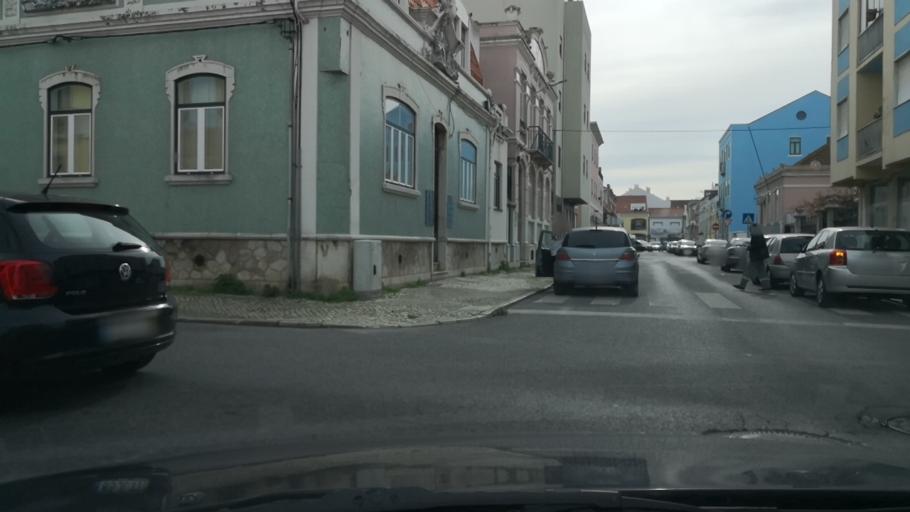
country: PT
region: Setubal
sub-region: Setubal
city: Setubal
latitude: 38.5277
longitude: -8.8875
